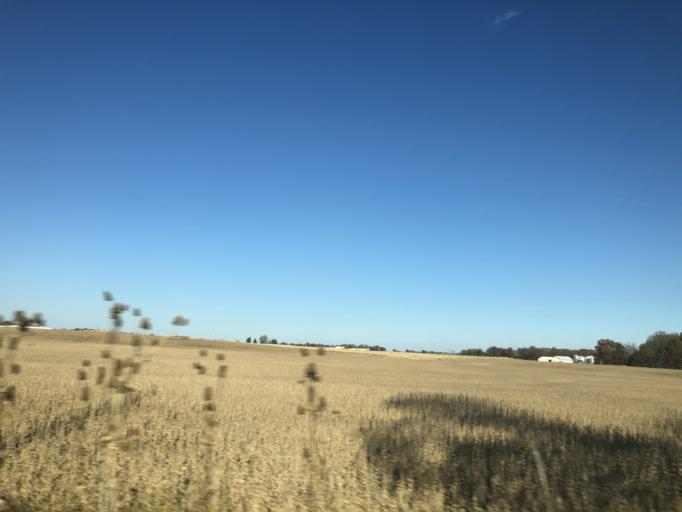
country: US
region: Indiana
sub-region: Allen County
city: Fort Wayne
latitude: 41.1105
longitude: -85.2212
